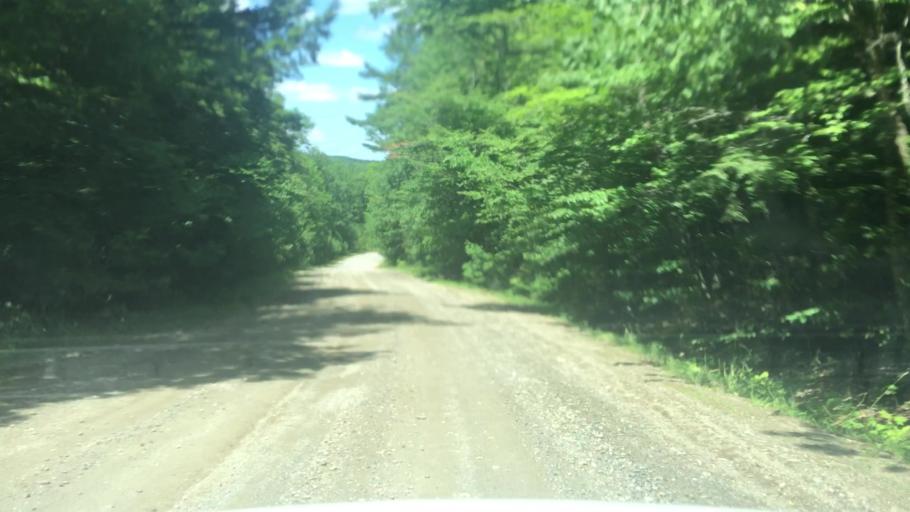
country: US
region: Maine
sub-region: Waldo County
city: Searsmont
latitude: 44.4751
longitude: -69.2985
